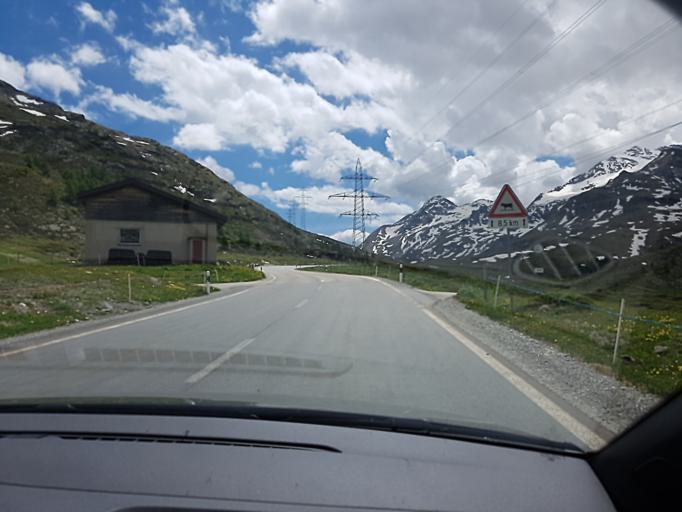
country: CH
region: Grisons
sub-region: Maloja District
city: Pontresina
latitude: 46.4351
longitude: 9.9958
